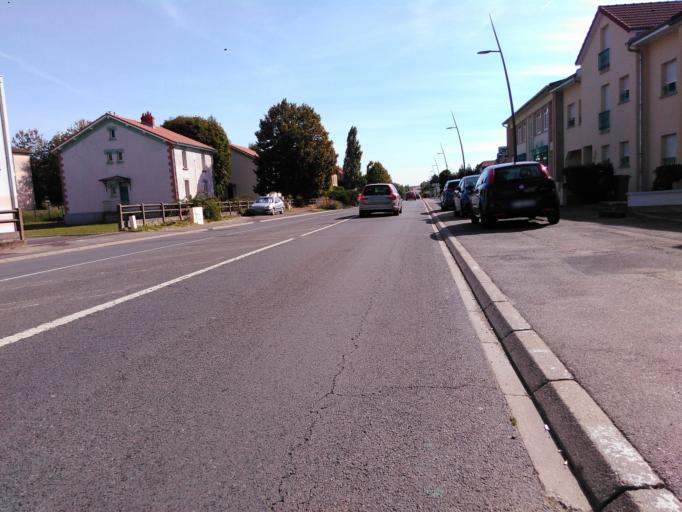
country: FR
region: Lorraine
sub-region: Departement de la Moselle
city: Hettange-Grande
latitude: 49.4003
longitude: 6.1603
